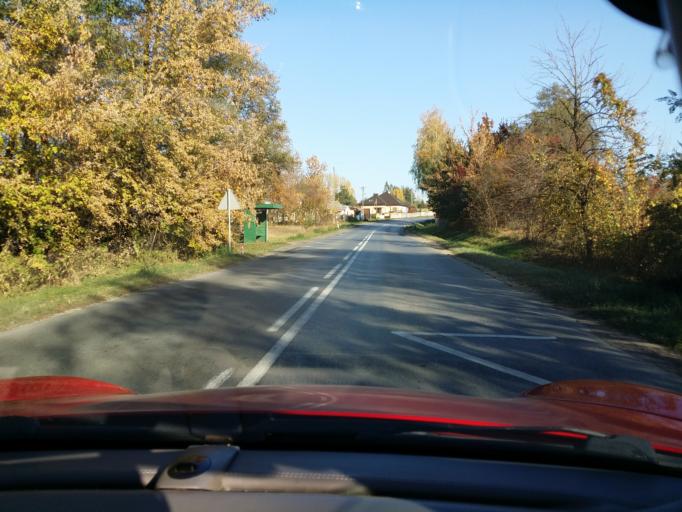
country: PL
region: Masovian Voivodeship
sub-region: Powiat szydlowiecki
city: Jastrzab
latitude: 51.2468
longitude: 20.9627
